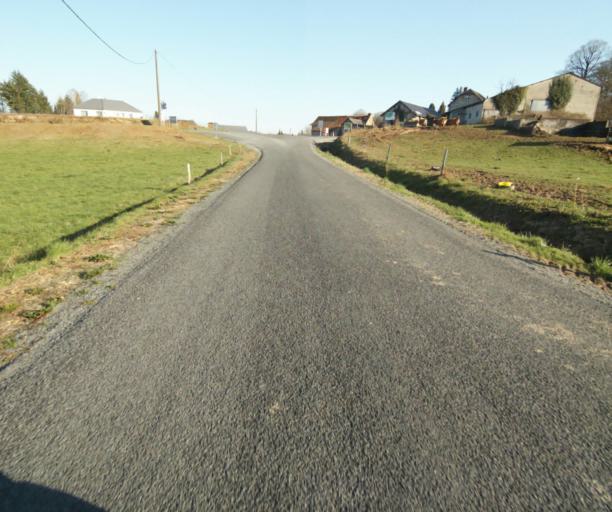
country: FR
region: Limousin
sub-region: Departement de la Correze
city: Saint-Clement
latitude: 45.3158
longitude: 1.6783
